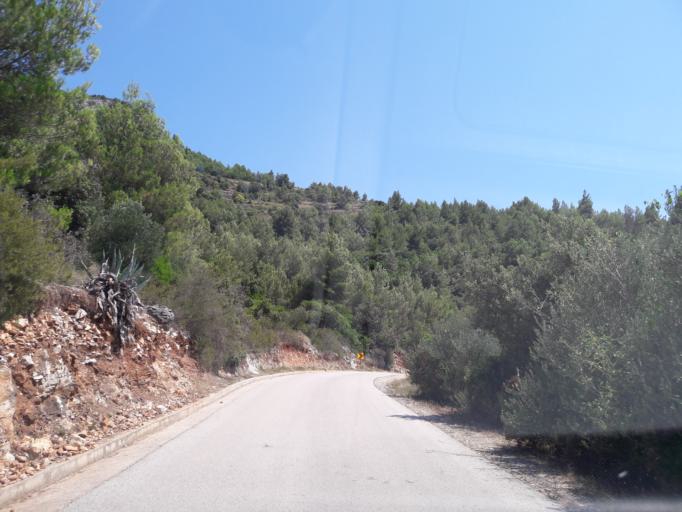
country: HR
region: Dubrovacko-Neretvanska
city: Blato
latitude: 42.9105
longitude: 17.4221
